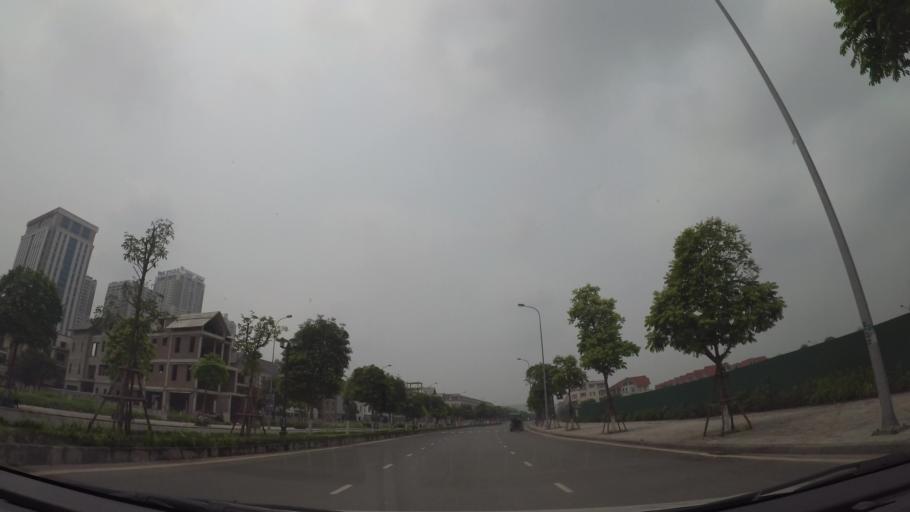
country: VN
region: Ha Noi
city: Ha Dong
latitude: 20.9768
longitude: 105.7574
